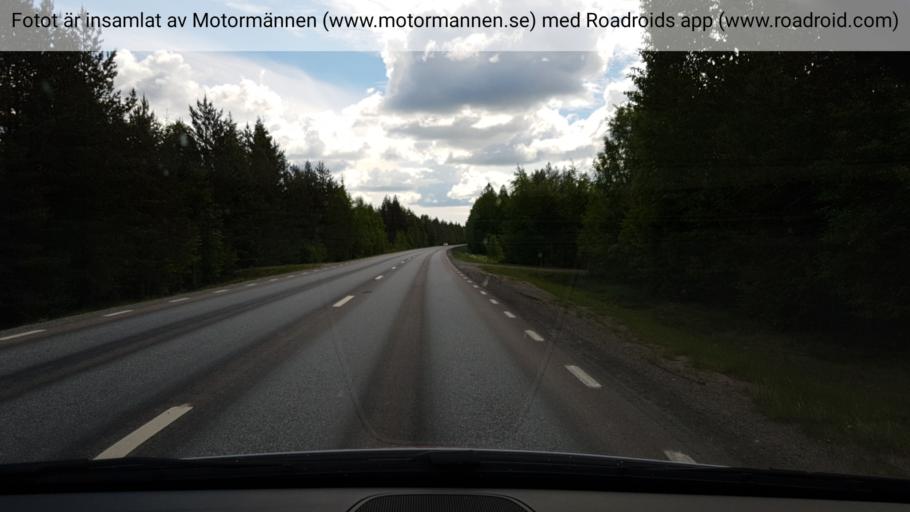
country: SE
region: Vaesterbotten
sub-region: Umea Kommun
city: Roback
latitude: 63.9605
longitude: 20.1314
